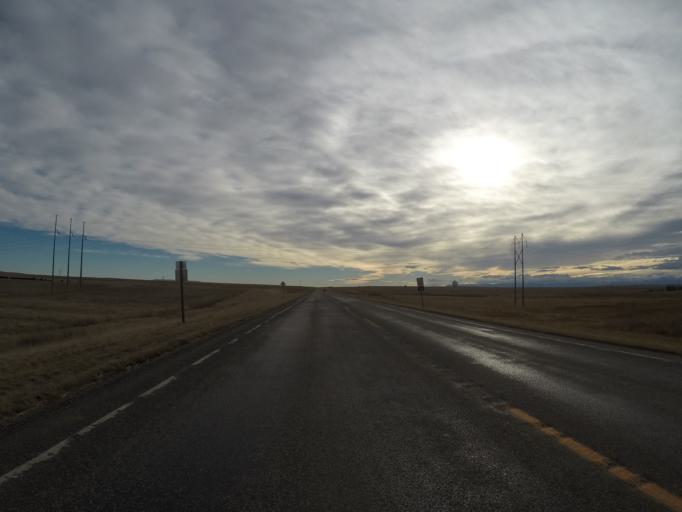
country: US
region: Montana
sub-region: Yellowstone County
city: Laurel
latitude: 45.8550
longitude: -108.8812
